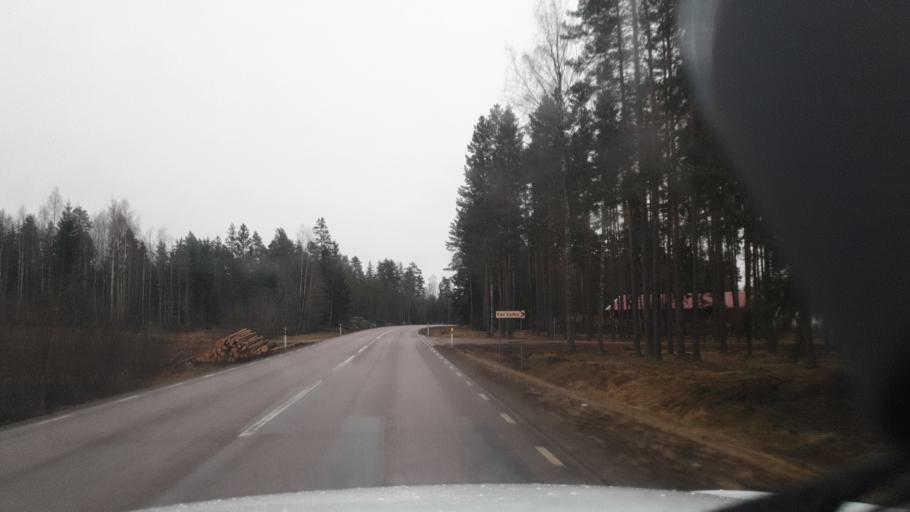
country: SE
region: Vaermland
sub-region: Eda Kommun
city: Charlottenberg
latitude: 59.8419
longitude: 12.3150
